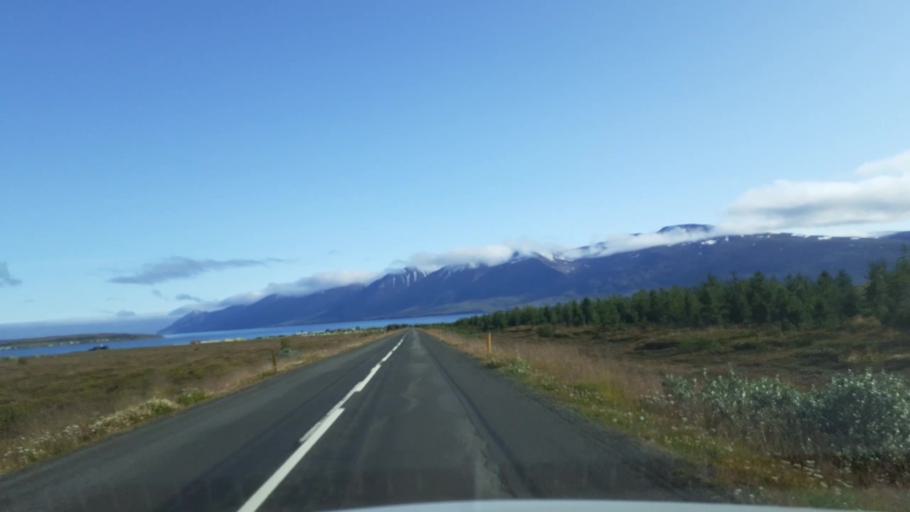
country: IS
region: Northeast
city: Dalvik
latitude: 65.9296
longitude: -18.3632
